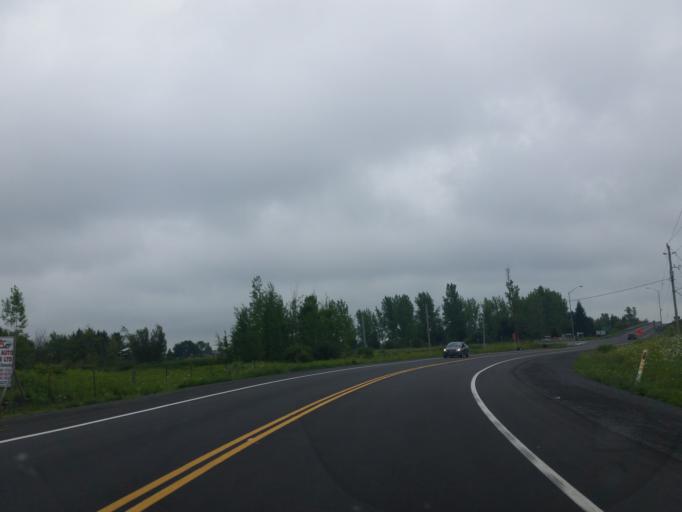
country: CA
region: Ontario
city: Bourget
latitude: 45.3400
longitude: -75.3444
